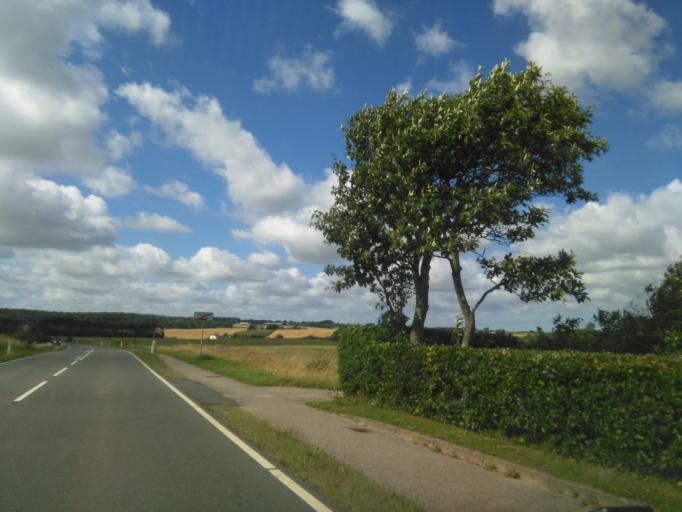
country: DK
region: Central Jutland
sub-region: Syddjurs Kommune
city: Ronde
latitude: 56.2722
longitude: 10.5137
